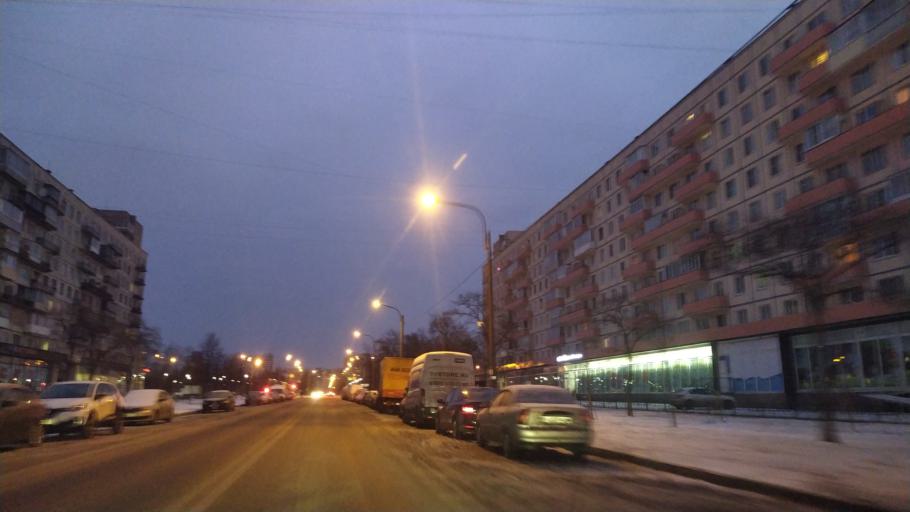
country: RU
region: Leningrad
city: Kalininskiy
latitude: 59.9630
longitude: 30.4156
